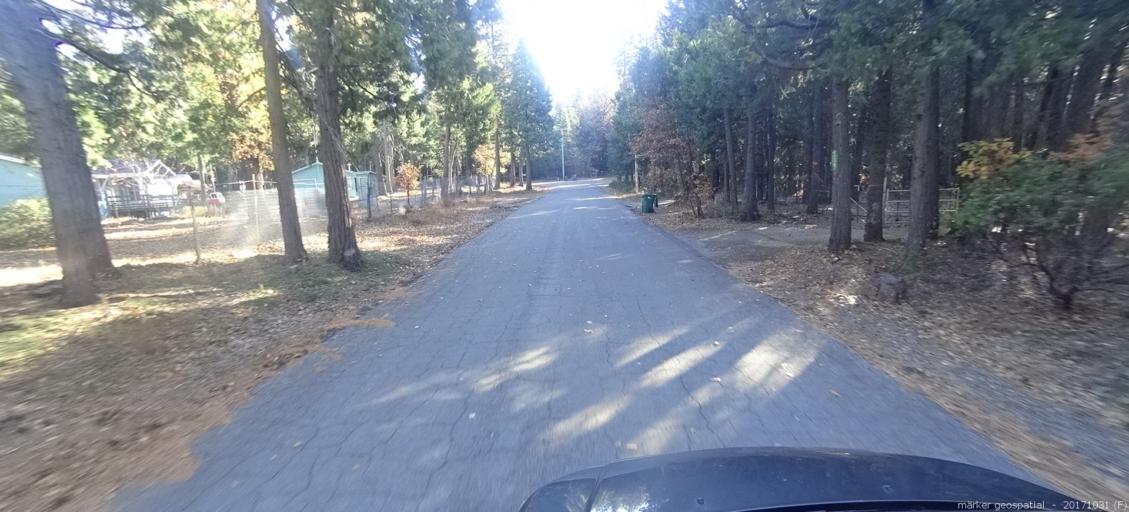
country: US
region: California
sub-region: Shasta County
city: Shingletown
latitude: 40.5273
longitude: -121.8346
